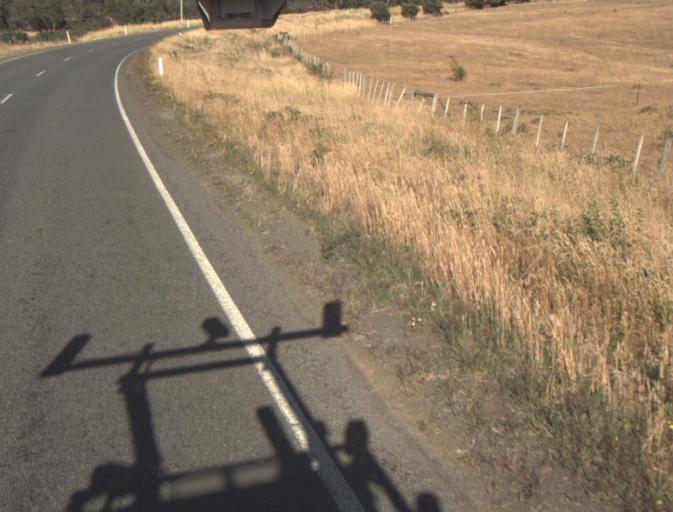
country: AU
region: Tasmania
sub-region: Launceston
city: Newstead
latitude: -41.4471
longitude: 147.2467
